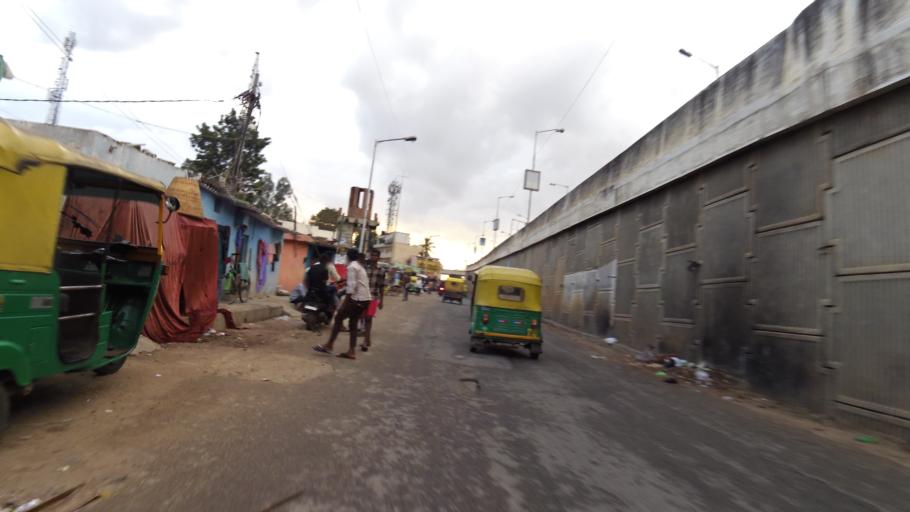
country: IN
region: Karnataka
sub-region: Bangalore Urban
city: Bangalore
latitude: 13.0032
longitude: 77.6376
